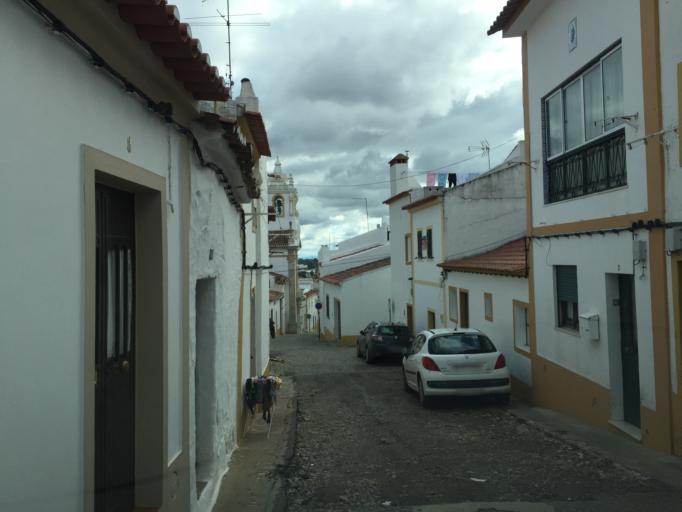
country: PT
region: Portalegre
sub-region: Alter do Chao
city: Alter do Chao
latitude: 39.2019
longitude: -7.6591
